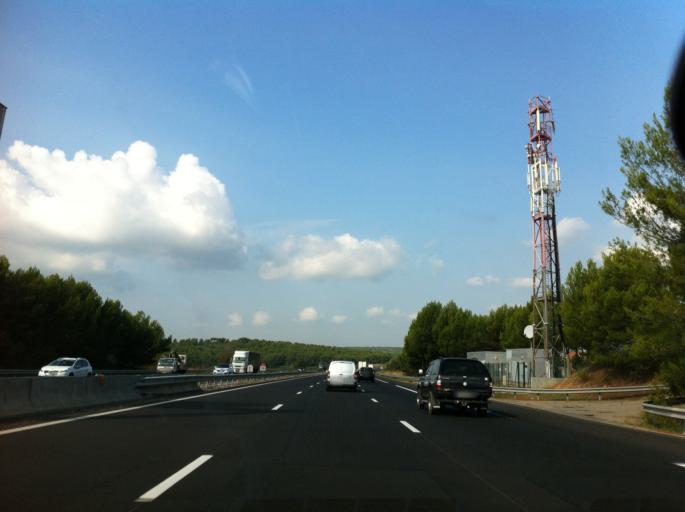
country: FR
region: Provence-Alpes-Cote d'Azur
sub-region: Departement des Bouches-du-Rhone
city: Eguilles
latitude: 43.5330
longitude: 5.3715
